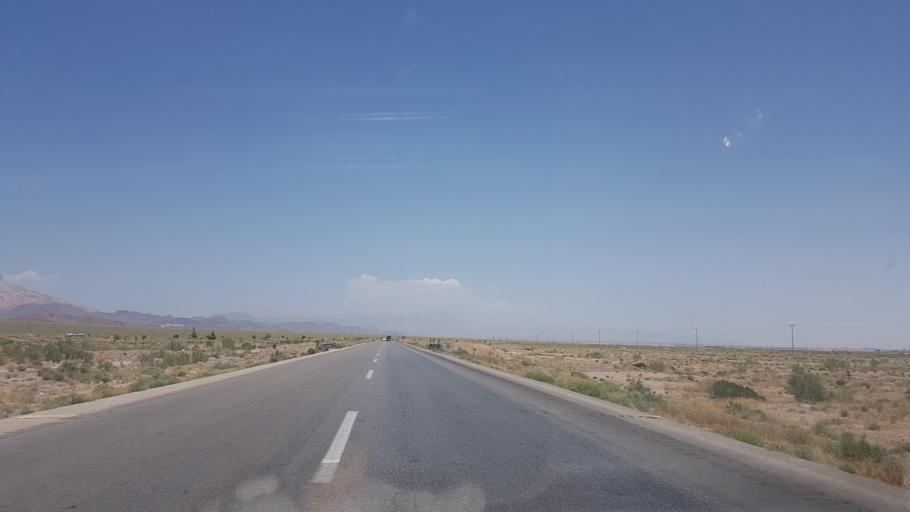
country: IR
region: Semnan
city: Damghan
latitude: 36.0396
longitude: 54.0997
